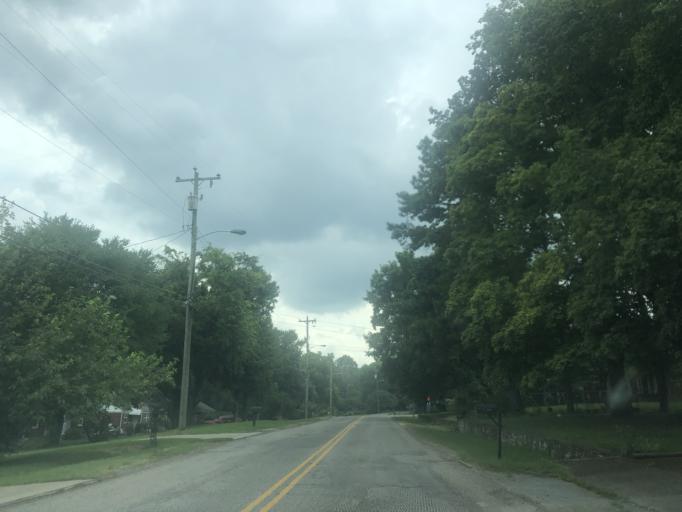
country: US
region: Tennessee
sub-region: Davidson County
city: Lakewood
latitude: 36.1668
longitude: -86.6824
